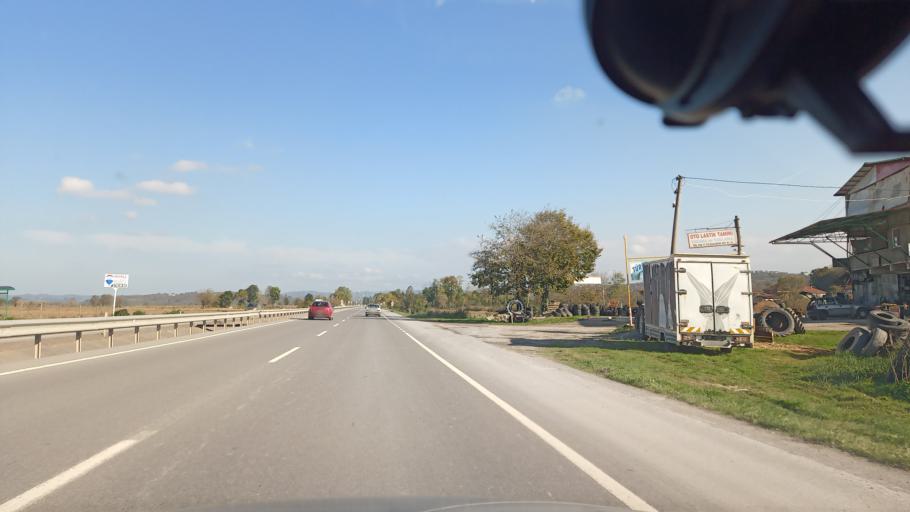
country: TR
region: Sakarya
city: Ferizli
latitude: 40.9793
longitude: 30.5258
